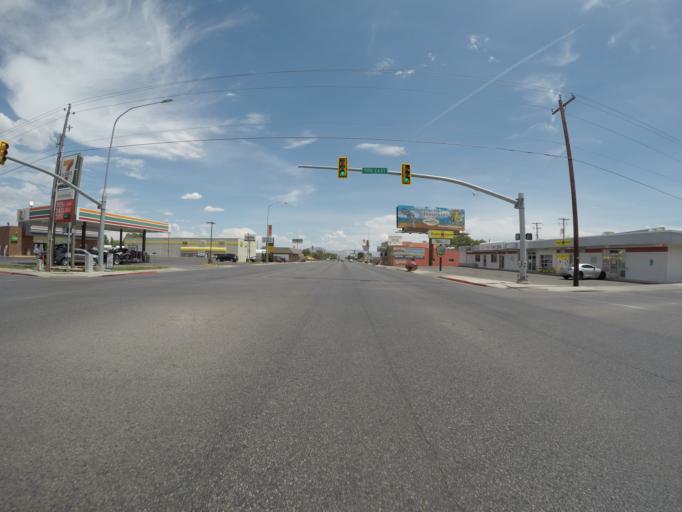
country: US
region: Utah
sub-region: Uintah County
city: Vernal
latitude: 40.4558
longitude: -109.5191
